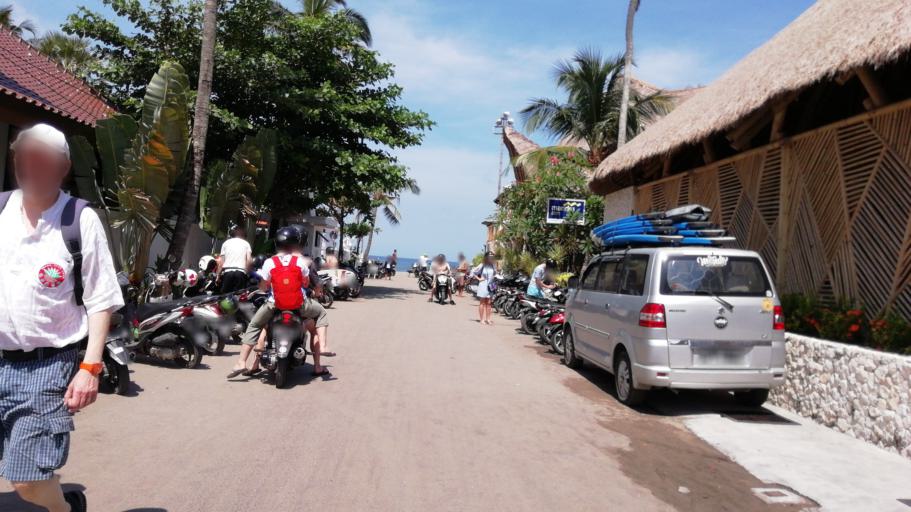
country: ID
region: Bali
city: Banjar Kerobokan
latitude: -8.6668
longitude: 115.1398
